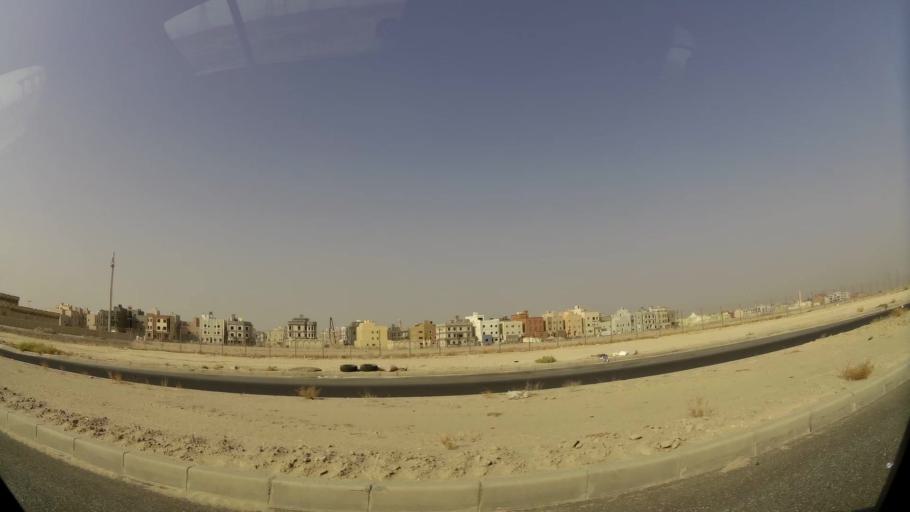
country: KW
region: Muhafazat al Jahra'
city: Al Jahra'
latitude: 29.3505
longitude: 47.7811
